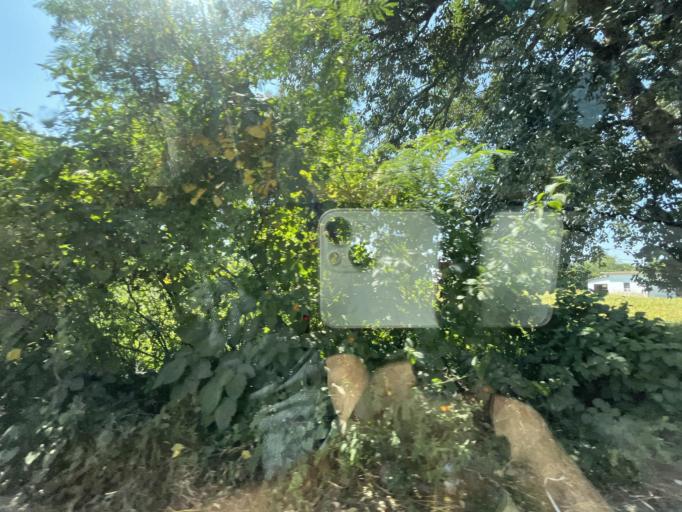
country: IN
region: Uttarakhand
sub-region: Naini Tal
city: Haldwani
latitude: 29.2138
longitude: 79.4542
